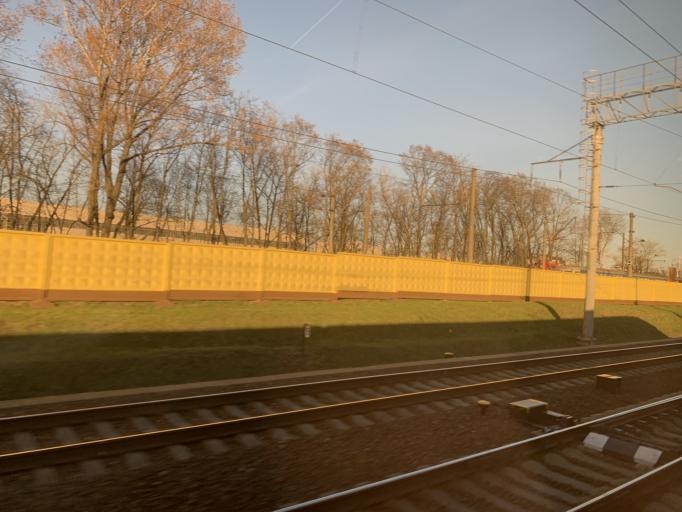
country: BY
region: Minsk
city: Minsk
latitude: 53.9193
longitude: 27.5145
